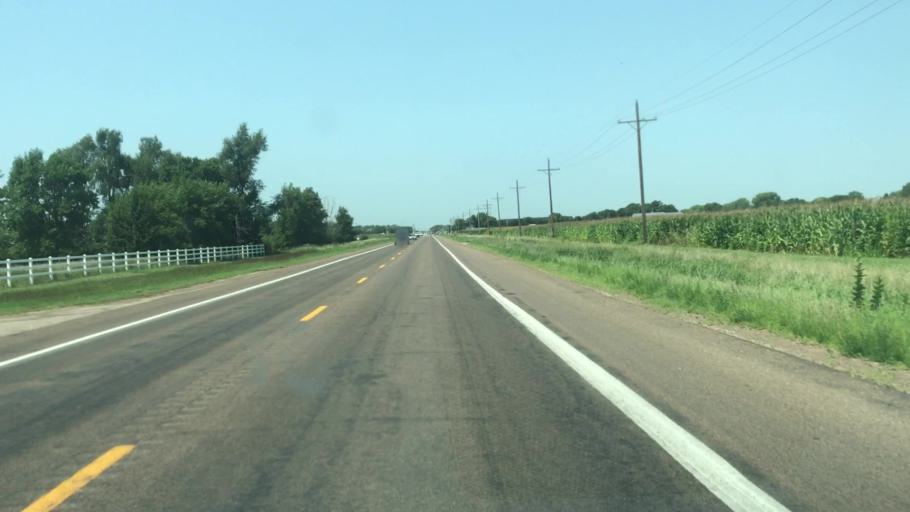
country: US
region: Nebraska
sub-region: Hall County
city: Grand Island
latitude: 40.8870
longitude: -98.3267
